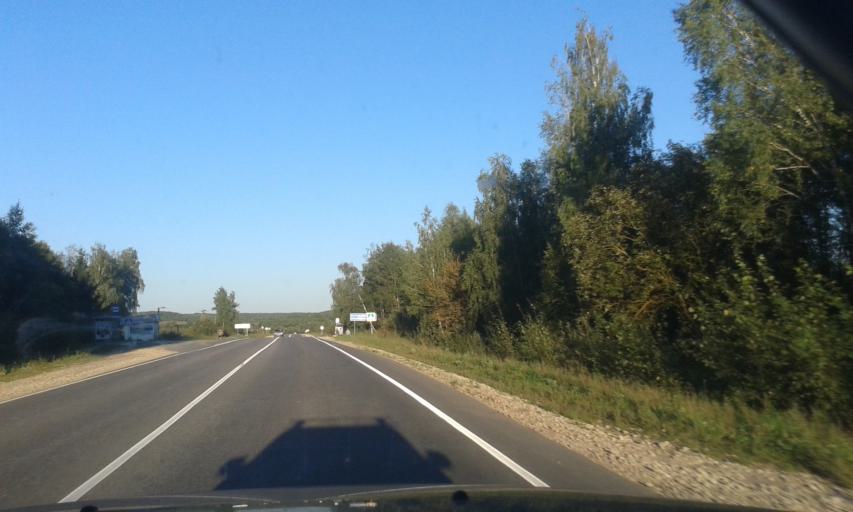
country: RU
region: Tula
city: Krapivna
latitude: 54.1125
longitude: 37.2036
